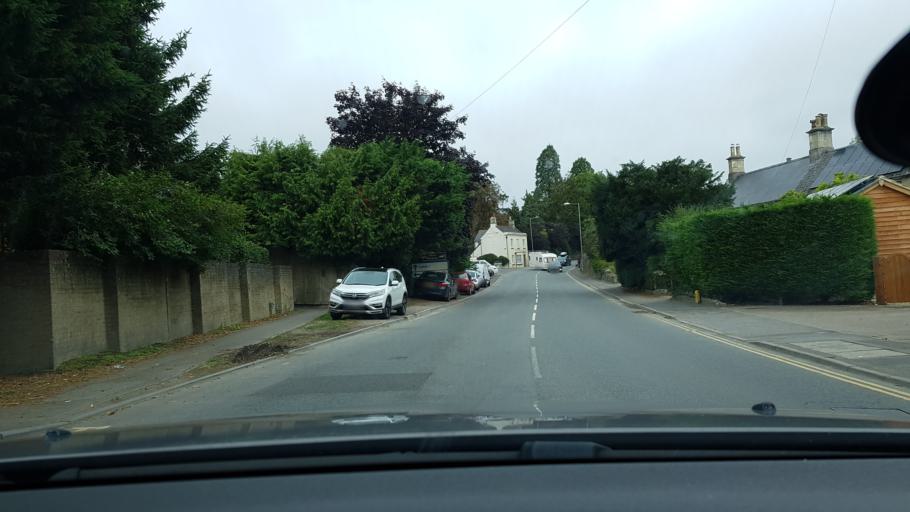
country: GB
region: England
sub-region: Wiltshire
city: Calne
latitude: 51.4270
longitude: -1.9923
